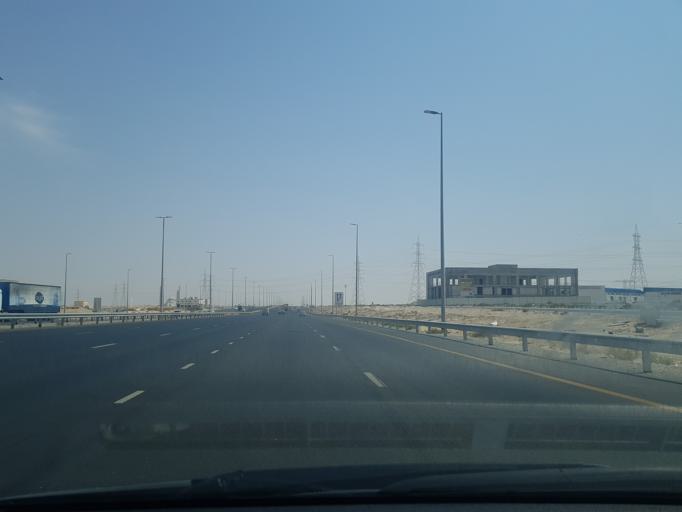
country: AE
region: Ash Shariqah
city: Sharjah
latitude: 25.2441
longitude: 55.5506
